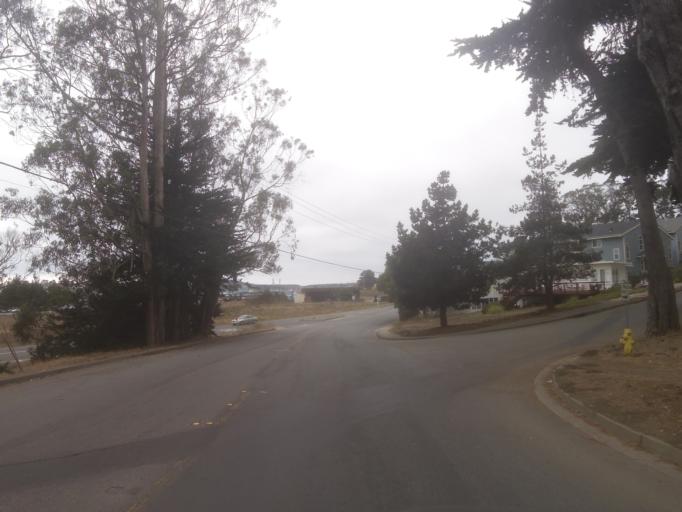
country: US
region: California
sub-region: San Mateo County
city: El Granada
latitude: 37.5031
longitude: -122.4719
